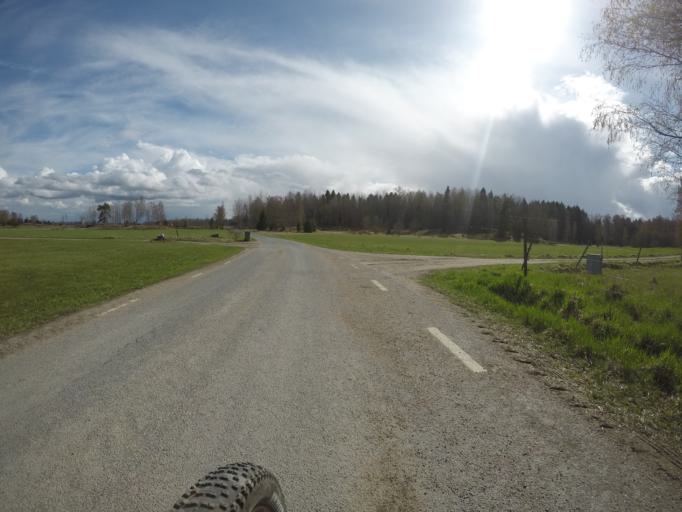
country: SE
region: Vaestmanland
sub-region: Kungsors Kommun
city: Kungsoer
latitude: 59.2967
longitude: 16.1413
